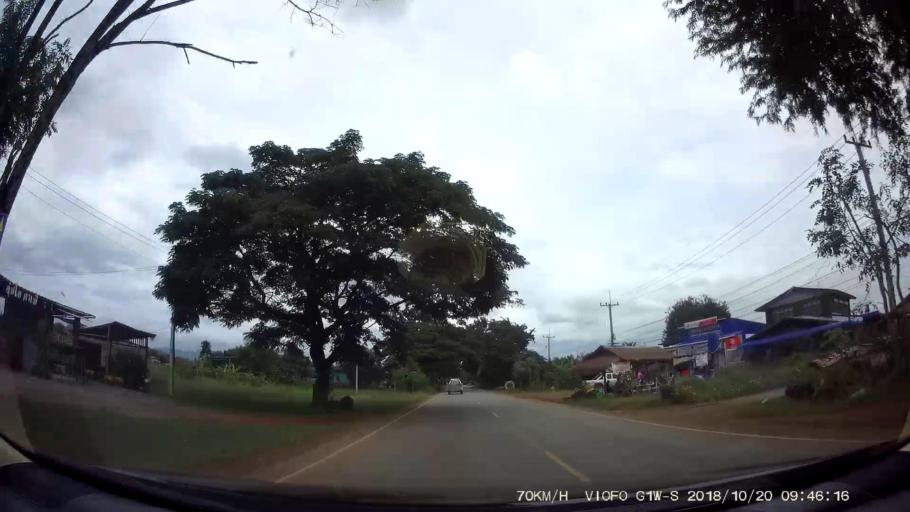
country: TH
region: Chaiyaphum
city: Khon San
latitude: 16.4950
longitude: 101.9281
